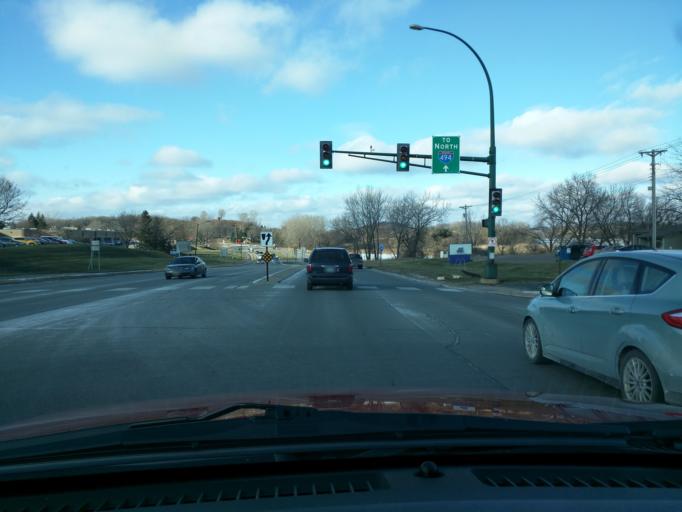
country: US
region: Minnesota
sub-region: Hennepin County
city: Eden Prairie
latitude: 44.8669
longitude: -93.4204
